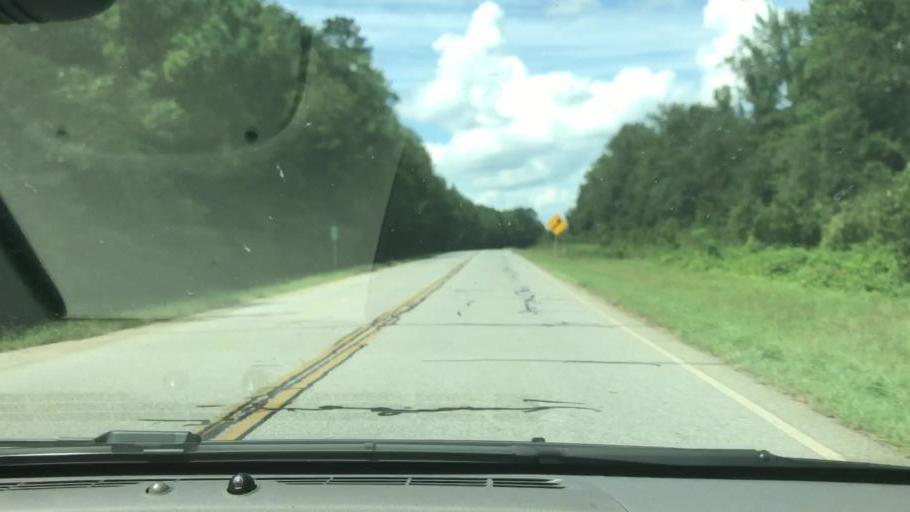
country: US
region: Georgia
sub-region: Stewart County
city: Lumpkin
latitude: 32.1472
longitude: -84.8964
